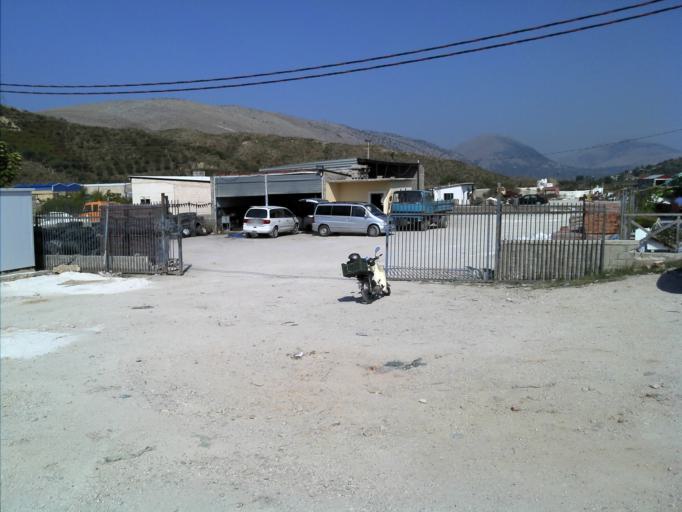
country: AL
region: Vlore
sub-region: Rrethi i Sarandes
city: Sarande
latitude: 39.8807
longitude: 20.0351
